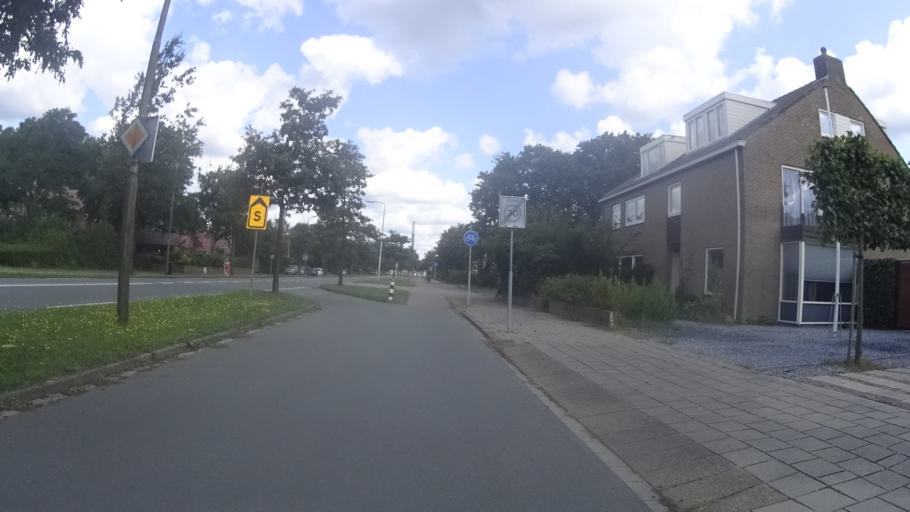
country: NL
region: North Holland
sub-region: Gemeente Velsen
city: Velsen-Zuid
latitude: 52.4581
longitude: 4.6335
